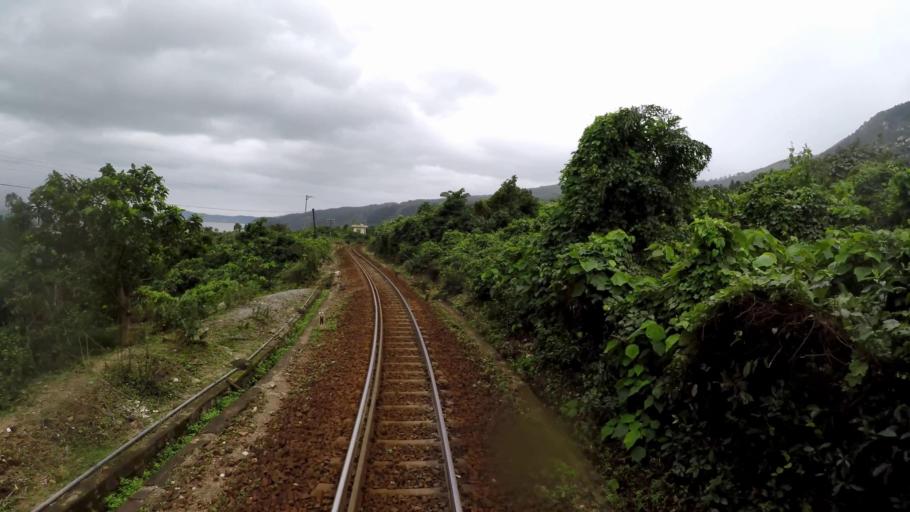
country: VN
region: Da Nang
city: Lien Chieu
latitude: 16.1695
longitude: 108.1365
